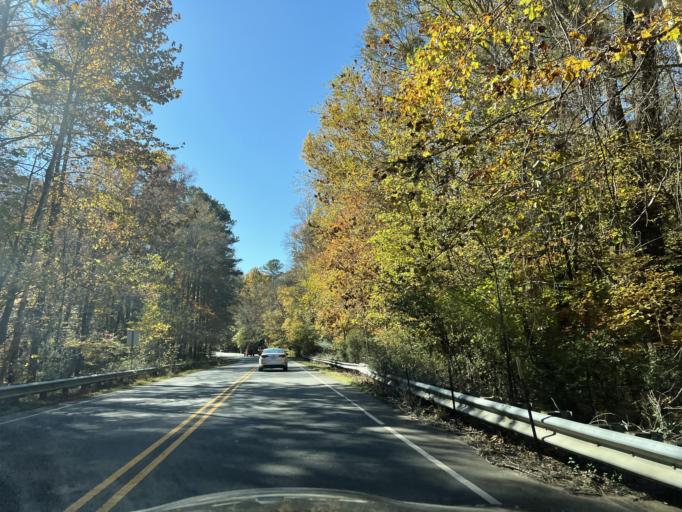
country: US
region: North Carolina
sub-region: Wake County
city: Fuquay-Varina
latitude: 35.6355
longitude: -78.7280
